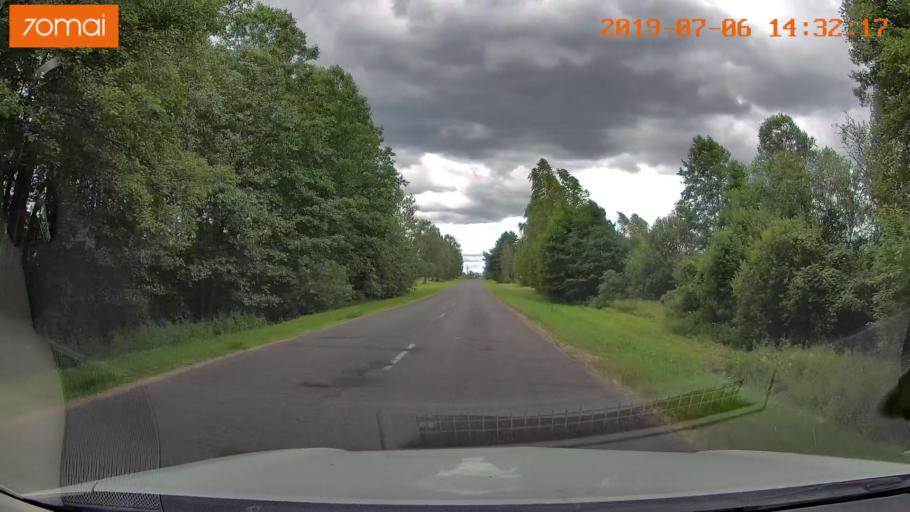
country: BY
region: Minsk
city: Ivyanyets
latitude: 53.9086
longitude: 26.7633
